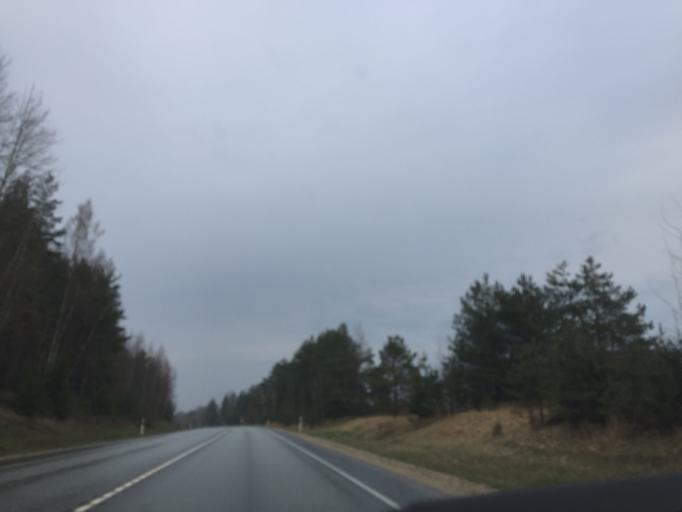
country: EE
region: Tartu
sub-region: UElenurme vald
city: Ulenurme
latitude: 58.1982
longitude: 26.7034
